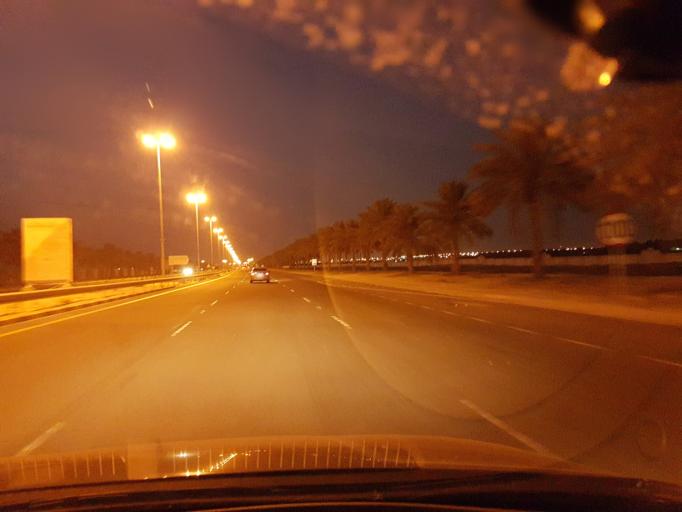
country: BH
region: Central Governorate
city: Dar Kulayb
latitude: 26.0392
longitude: 50.5000
